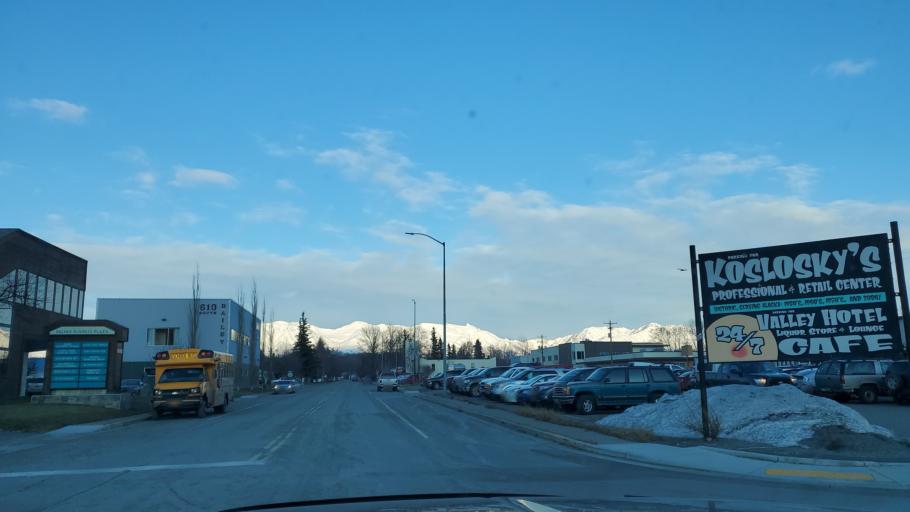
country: US
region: Alaska
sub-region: Matanuska-Susitna Borough
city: Palmer
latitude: 61.6004
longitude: -149.1165
